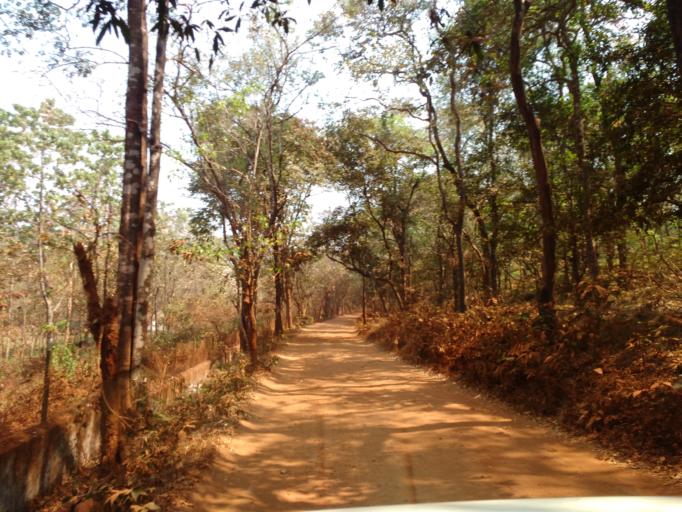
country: IN
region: Goa
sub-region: South Goa
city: Sanguem
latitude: 15.3408
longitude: 74.2512
